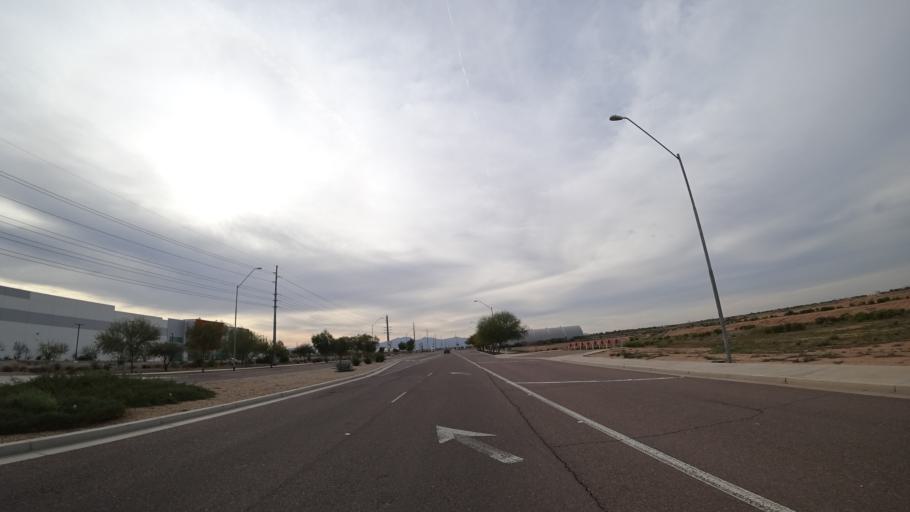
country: US
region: Arizona
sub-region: Maricopa County
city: El Mirage
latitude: 33.5947
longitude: -112.3483
